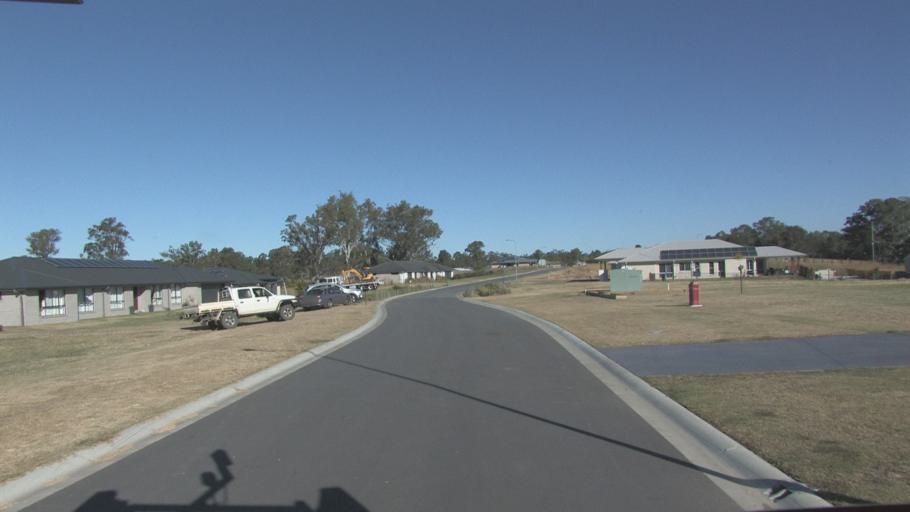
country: AU
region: Queensland
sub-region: Logan
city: North Maclean
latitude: -27.7840
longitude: 153.0254
